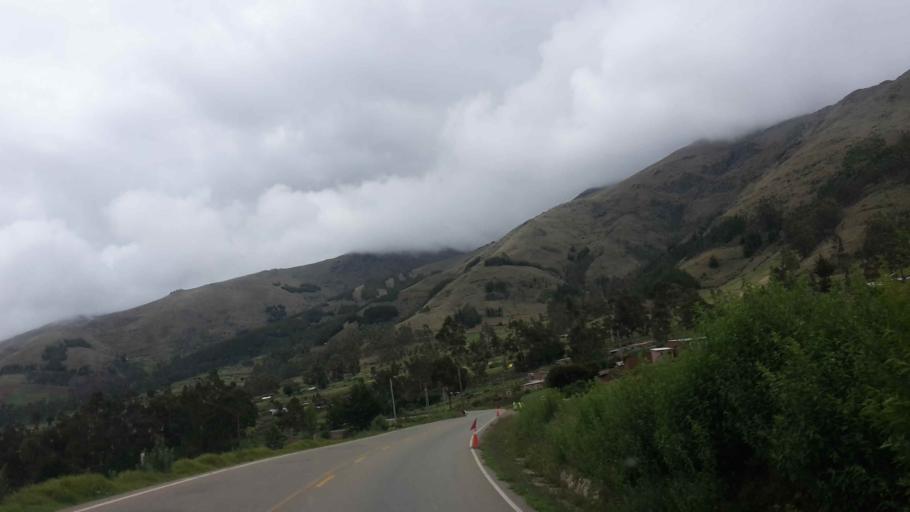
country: BO
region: Cochabamba
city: Arani
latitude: -17.4836
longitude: -65.4784
